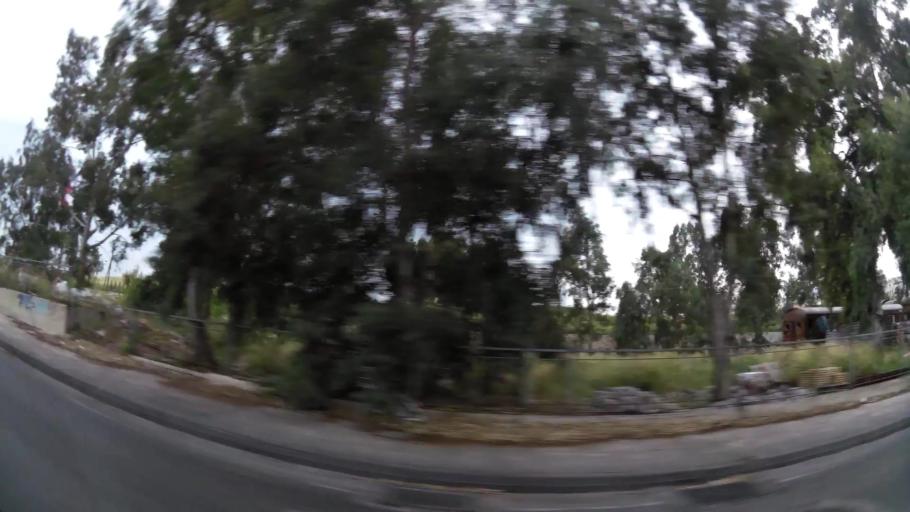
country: GR
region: Attica
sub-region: Nomos Attikis
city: Piraeus
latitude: 37.9478
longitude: 23.6359
